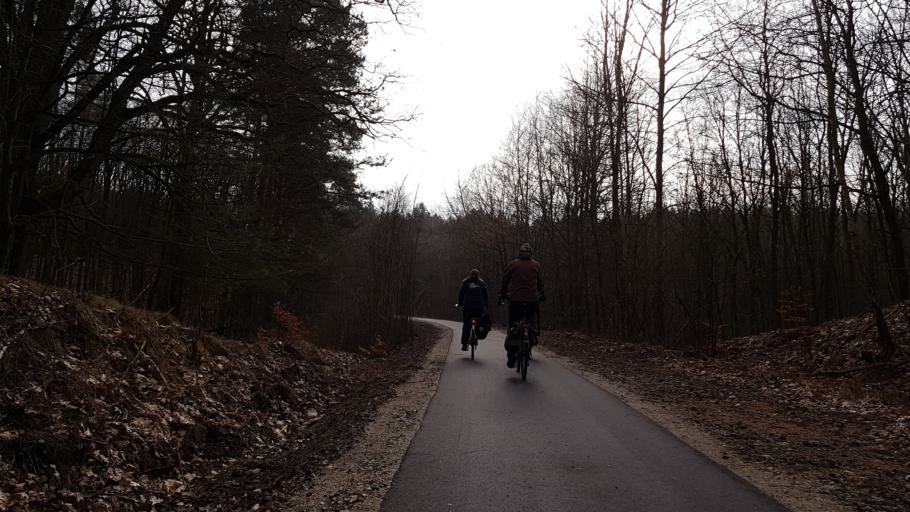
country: PL
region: West Pomeranian Voivodeship
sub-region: Powiat mysliborski
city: Barlinek
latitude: 53.0107
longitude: 15.2405
